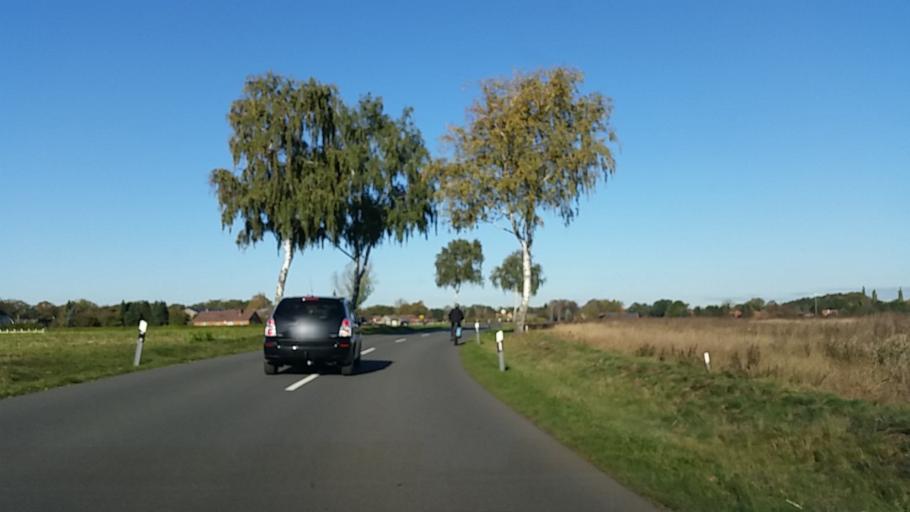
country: DE
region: Lower Saxony
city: Luder
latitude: 52.8039
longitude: 10.6720
